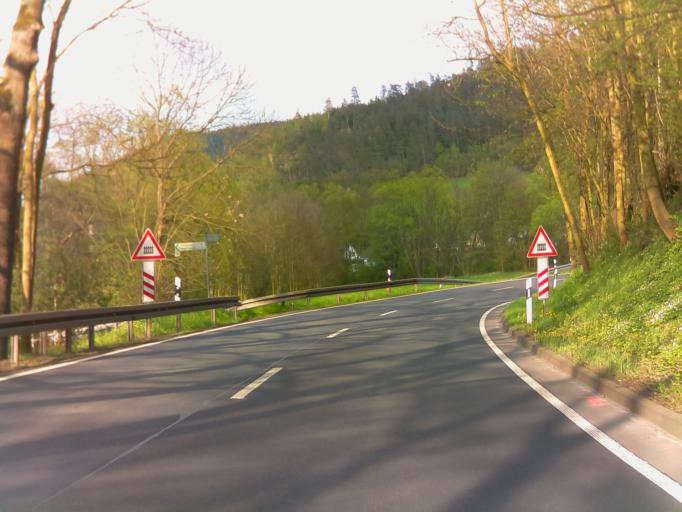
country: DE
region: Thuringia
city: Kaulsdorf
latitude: 50.5939
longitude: 11.4294
